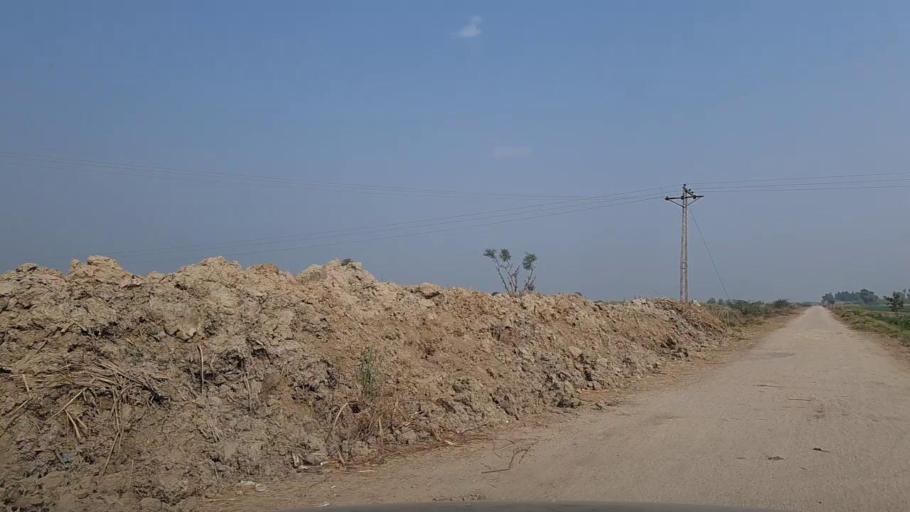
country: PK
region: Sindh
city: Nawabshah
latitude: 26.2769
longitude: 68.4315
